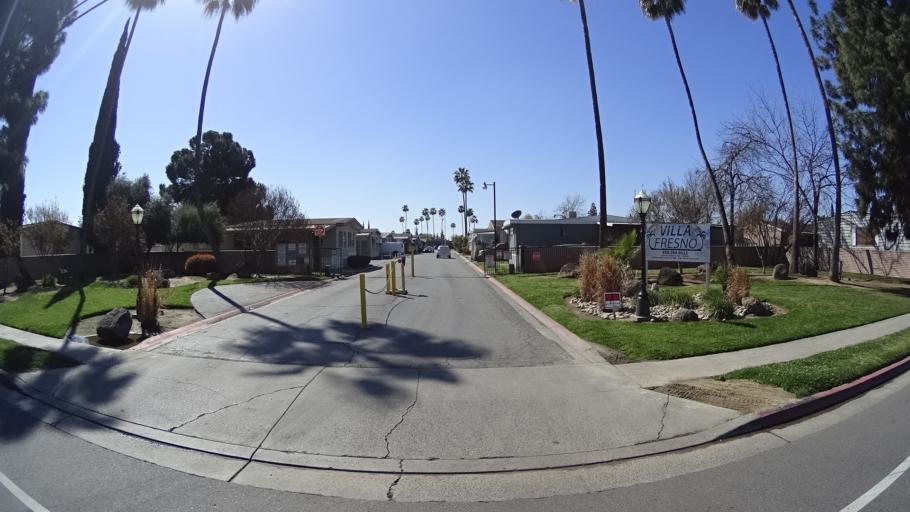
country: US
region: California
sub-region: Fresno County
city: West Park
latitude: 36.7646
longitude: -119.8416
